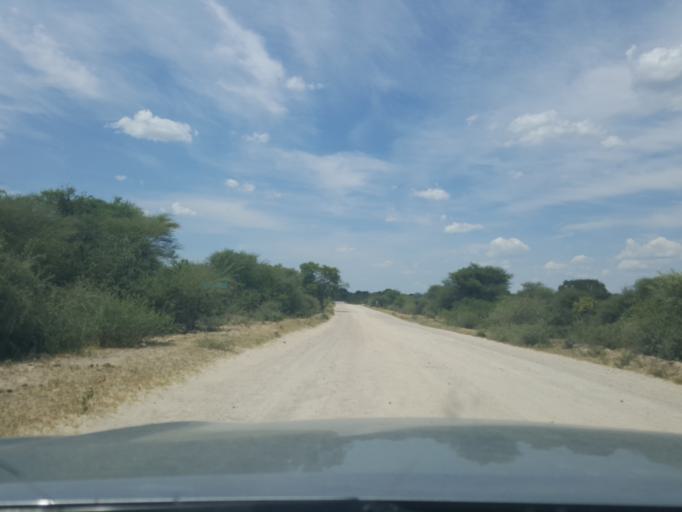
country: BW
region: North West
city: Shakawe
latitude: -18.3207
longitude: 21.9139
